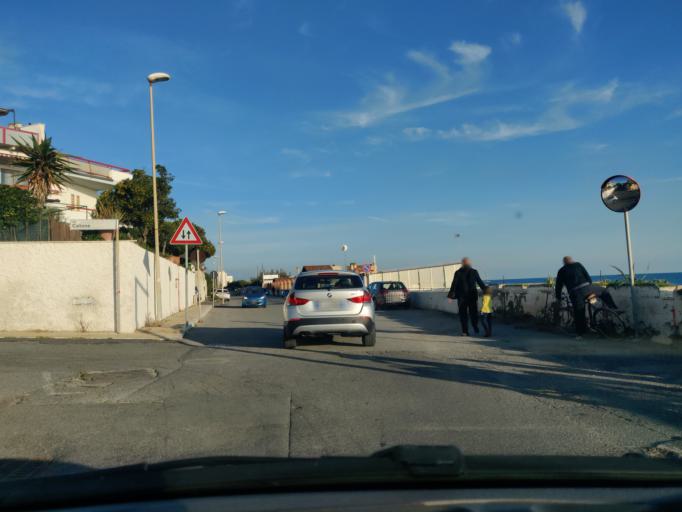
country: IT
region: Latium
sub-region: Citta metropolitana di Roma Capitale
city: Santa Marinella
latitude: 42.0297
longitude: 11.8366
